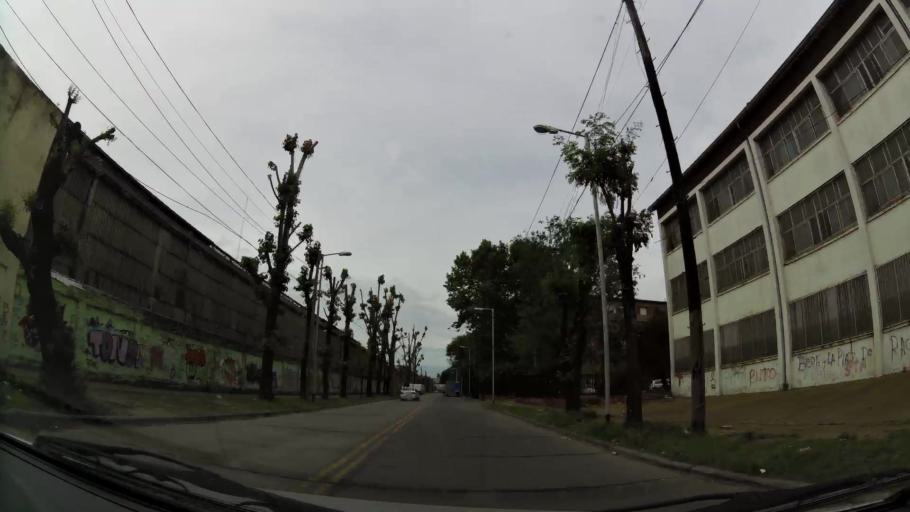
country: AR
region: Buenos Aires
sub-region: Partido de Avellaneda
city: Avellaneda
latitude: -34.6648
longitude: -58.3745
